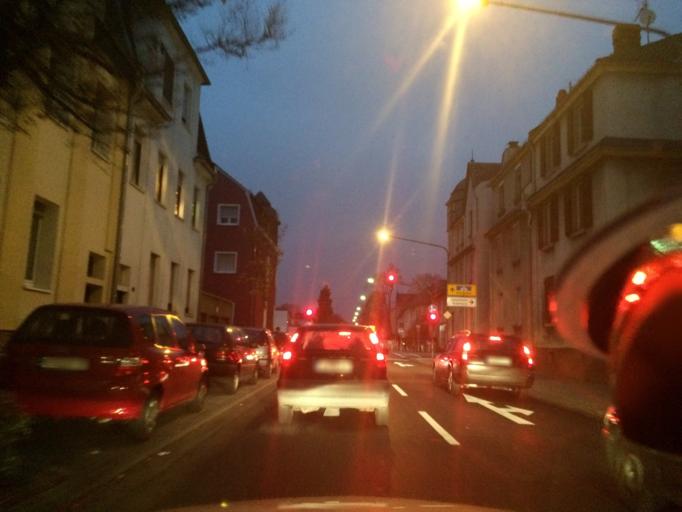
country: DE
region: Hesse
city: Sulzbach
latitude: 50.1115
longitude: 8.5396
